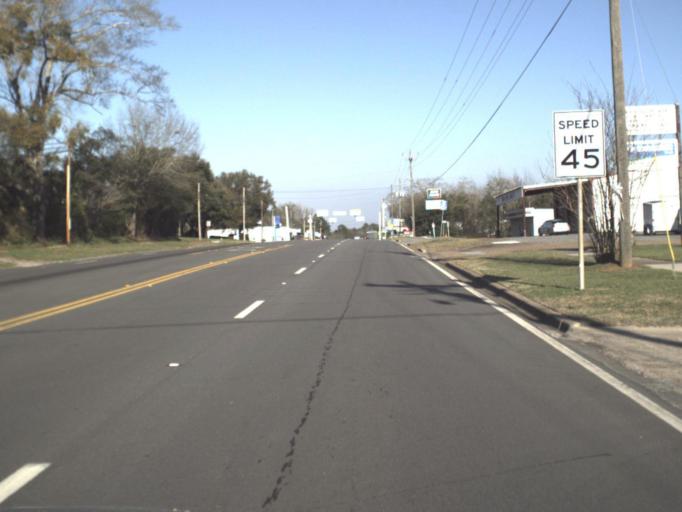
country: US
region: Florida
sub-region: Jackson County
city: Sneads
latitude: 30.7100
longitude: -84.9281
